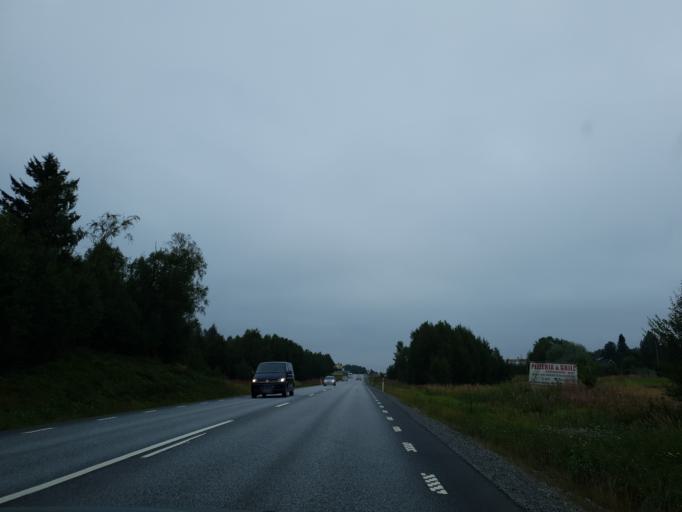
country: SE
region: Vaesterbotten
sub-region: Robertsfors Kommun
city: Robertsfors
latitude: 64.2257
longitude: 21.0160
